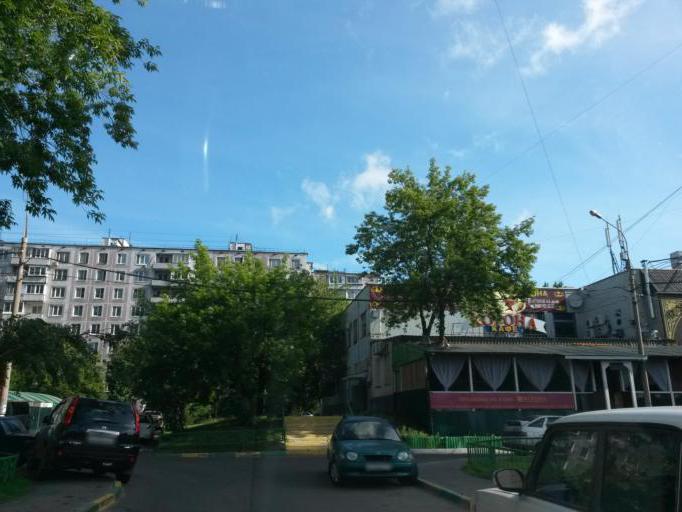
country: RU
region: Moscow
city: Mar'ino
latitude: 55.6434
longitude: 37.7240
